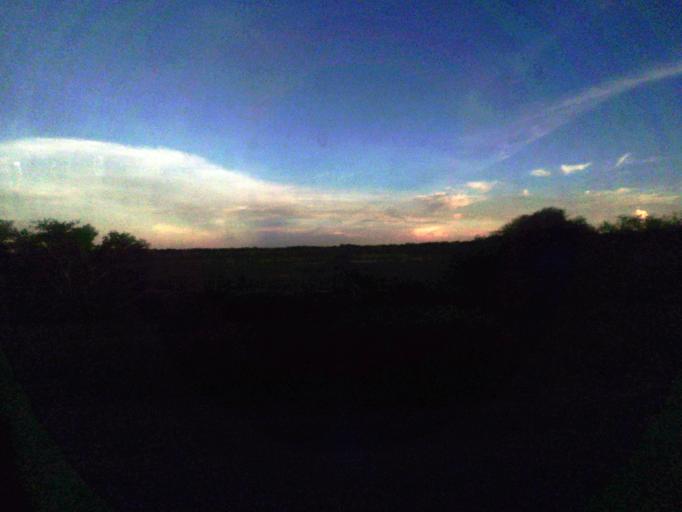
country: BO
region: Santa Cruz
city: Abapo
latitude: -18.4813
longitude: -63.2155
